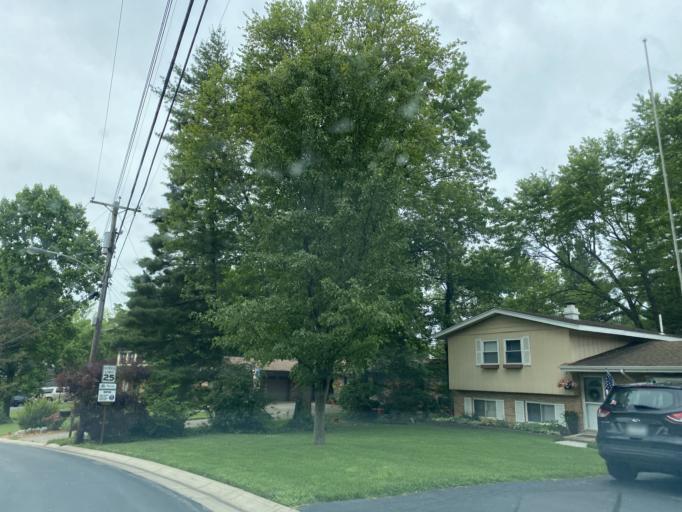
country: US
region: Ohio
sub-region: Hamilton County
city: Salem Heights
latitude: 39.0863
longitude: -84.4029
